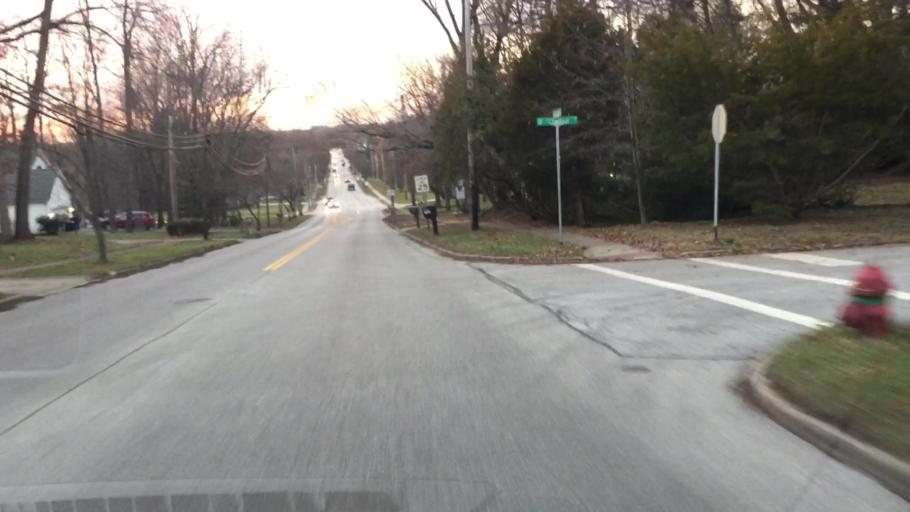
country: US
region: Ohio
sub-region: Portage County
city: Kent
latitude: 41.1606
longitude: -81.3660
